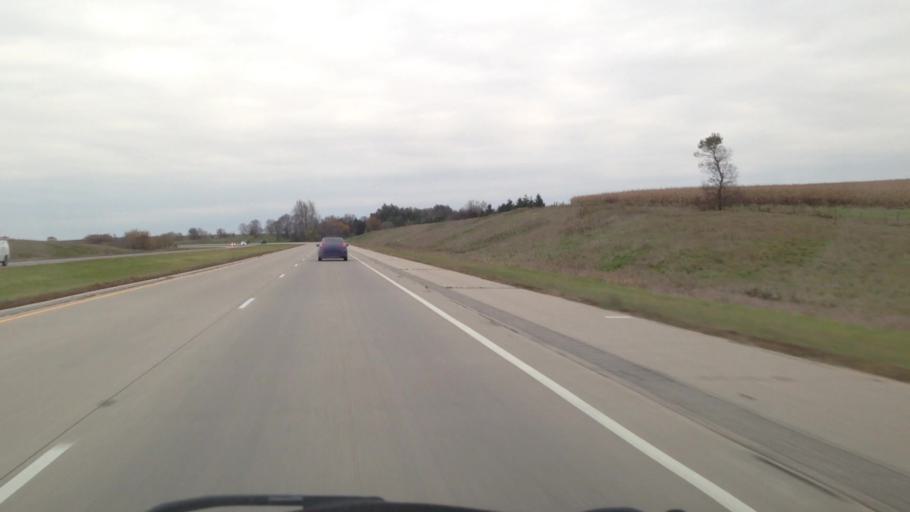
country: US
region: Minnesota
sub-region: Winona County
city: Saint Charles
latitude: 43.9379
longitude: -92.0163
